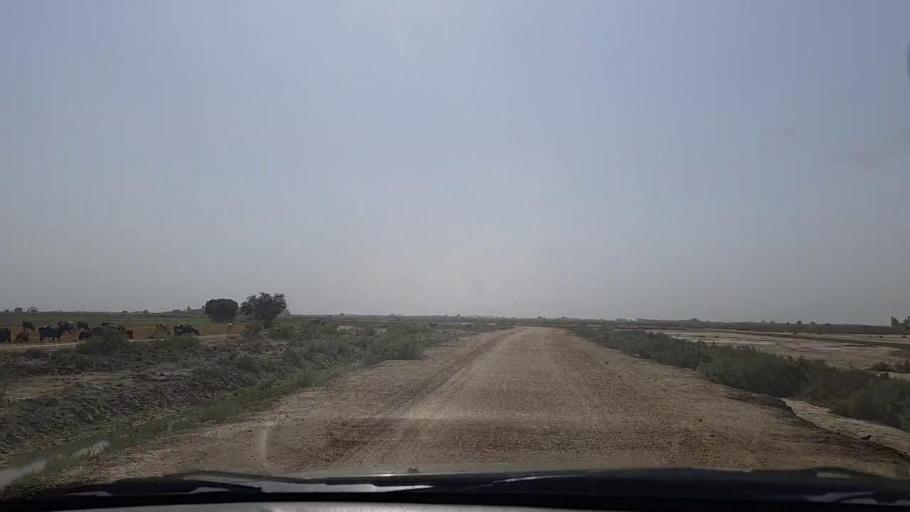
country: PK
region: Sindh
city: Keti Bandar
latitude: 24.2666
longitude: 67.6690
